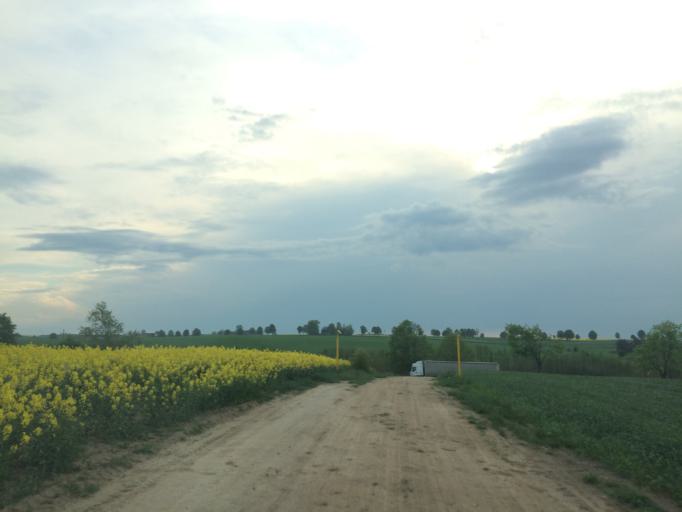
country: PL
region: Warmian-Masurian Voivodeship
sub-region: Powiat nowomiejski
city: Kurzetnik
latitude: 53.3559
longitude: 19.5725
